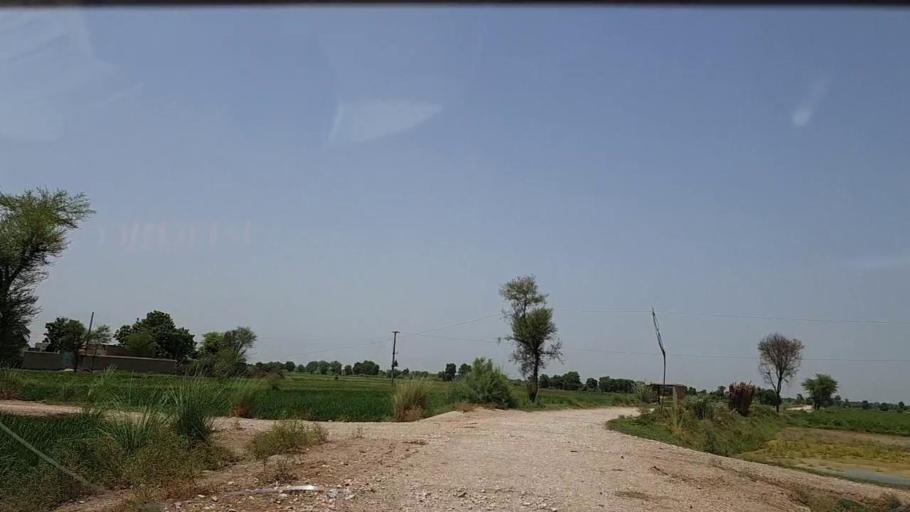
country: PK
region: Sindh
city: Tharu Shah
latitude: 26.9487
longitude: 68.0439
